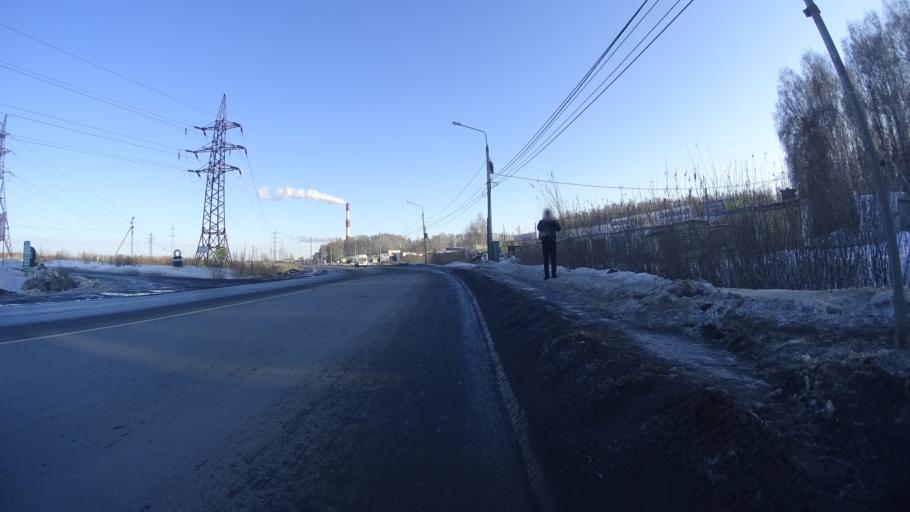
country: RU
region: Chelyabinsk
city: Roshchino
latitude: 55.2115
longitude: 61.3088
